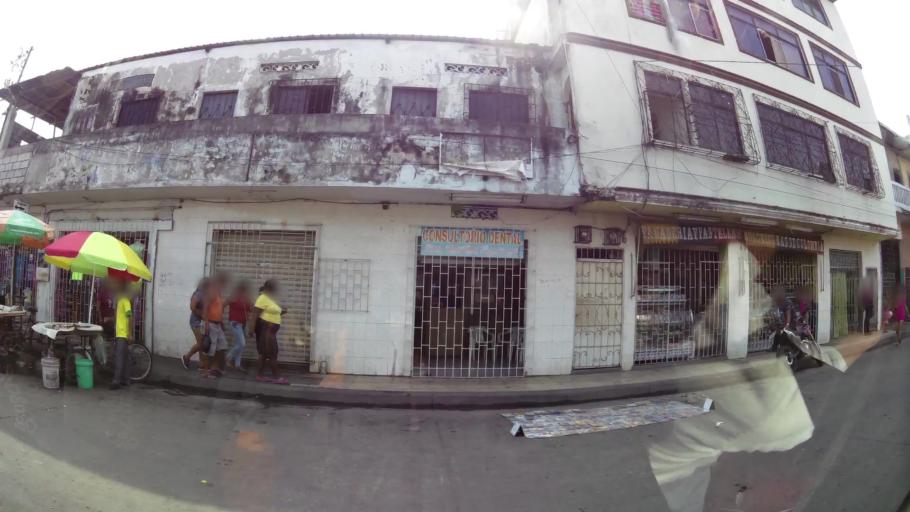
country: EC
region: Guayas
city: Guayaquil
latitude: -2.2798
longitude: -79.8814
